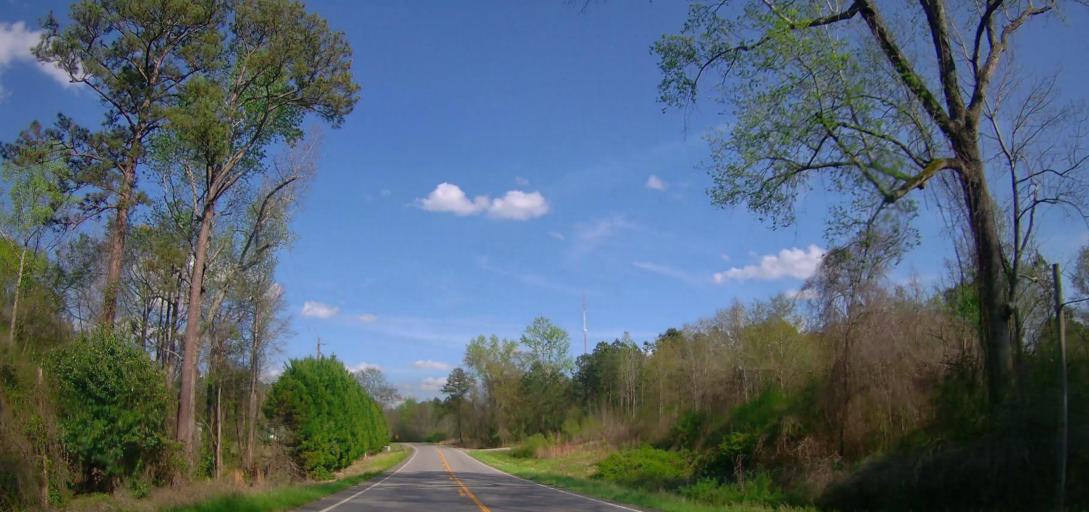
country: US
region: Georgia
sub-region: Baldwin County
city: Hardwick
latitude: 33.0799
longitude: -83.1548
